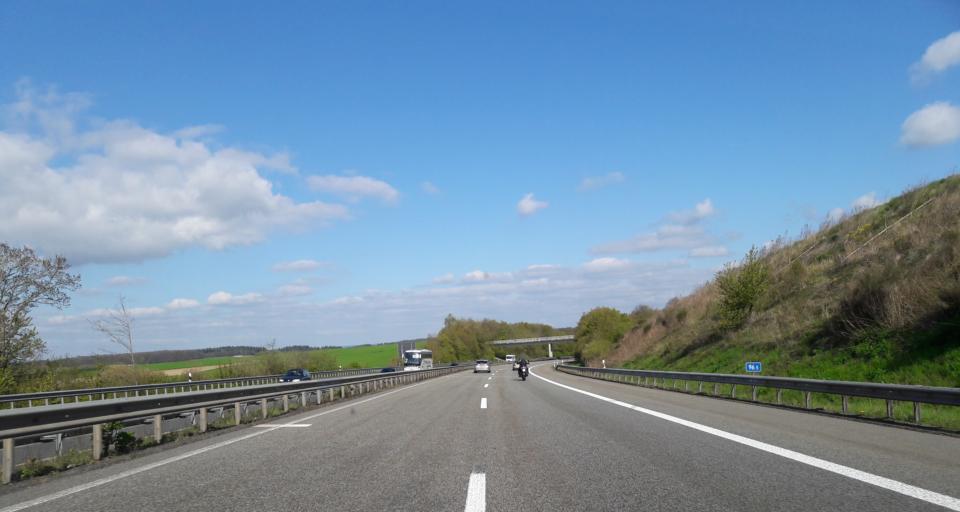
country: DE
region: Rheinland-Pfalz
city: Hasborn
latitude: 50.0486
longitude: 6.9095
